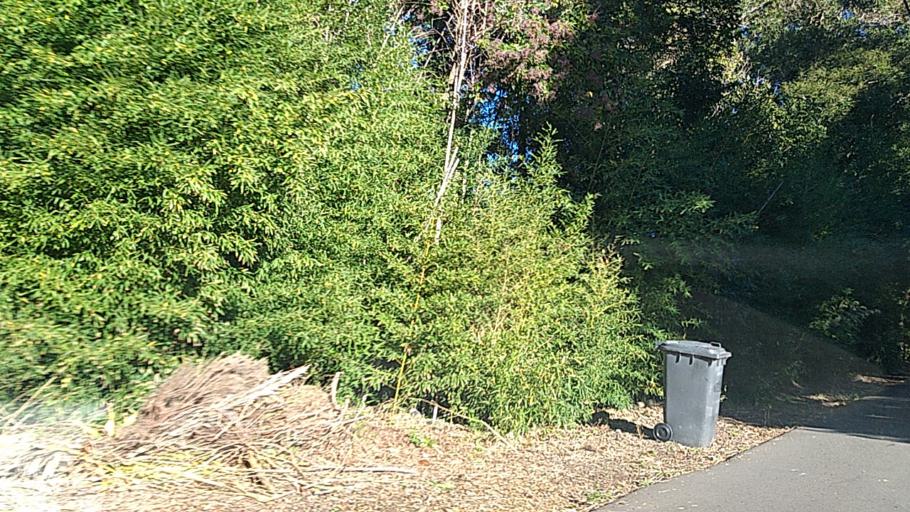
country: AU
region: New South Wales
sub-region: Wollongong
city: Bulli
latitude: -34.3119
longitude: 150.9193
